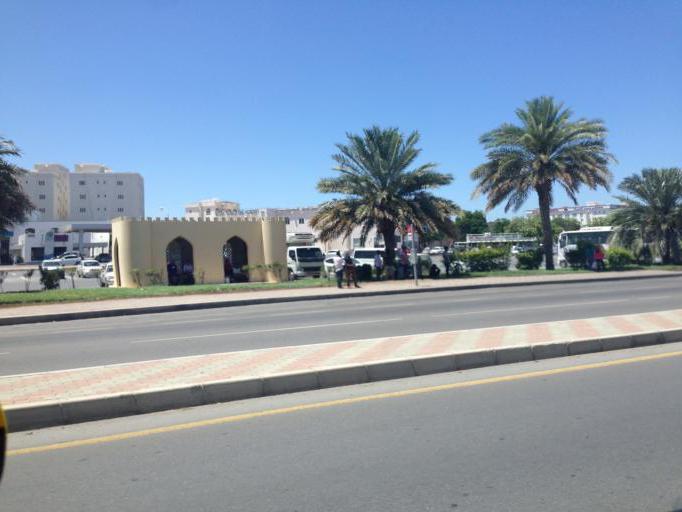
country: OM
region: Muhafazat Masqat
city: As Sib al Jadidah
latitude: 23.6512
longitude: 58.2046
